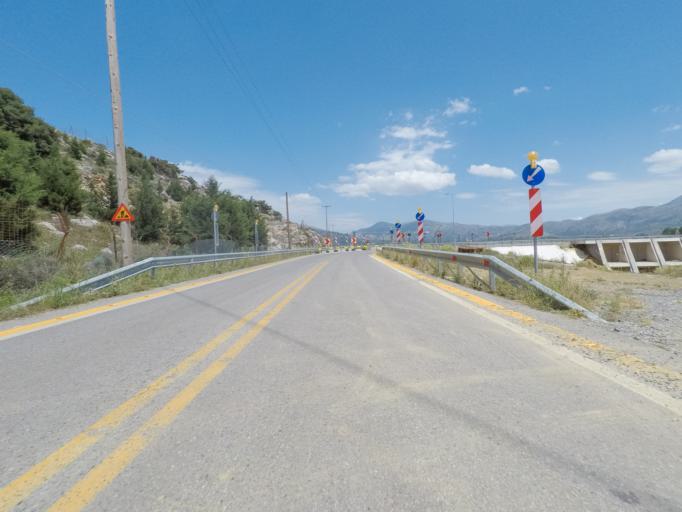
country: GR
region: Crete
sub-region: Nomos Irakleiou
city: Mokhos
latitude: 35.1946
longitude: 25.4415
